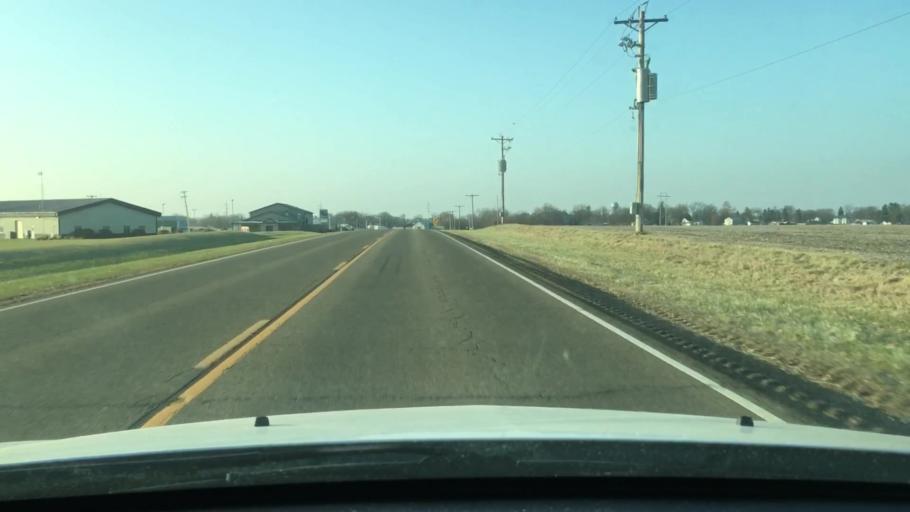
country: US
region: Illinois
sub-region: Woodford County
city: Washburn
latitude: 40.9292
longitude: -89.2822
